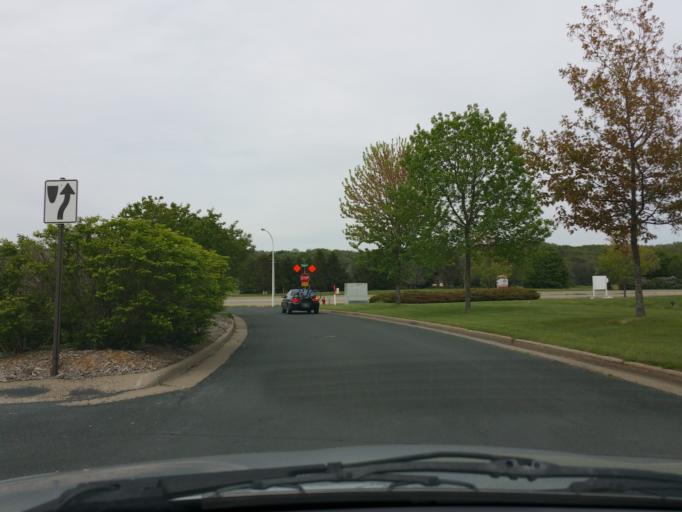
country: US
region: Wisconsin
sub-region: Pierce County
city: River Falls
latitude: 44.8873
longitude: -92.6316
